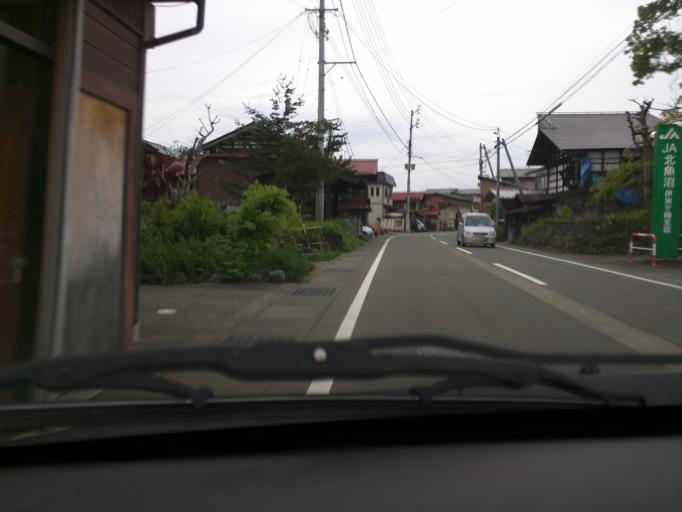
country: JP
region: Niigata
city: Muikamachi
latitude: 37.1991
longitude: 138.9518
